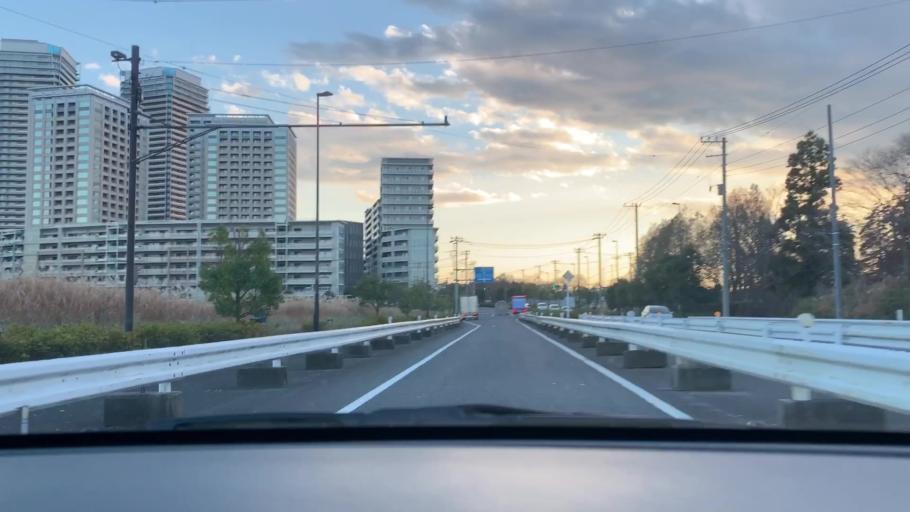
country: JP
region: Chiba
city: Kashiwa
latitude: 35.8996
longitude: 139.9498
